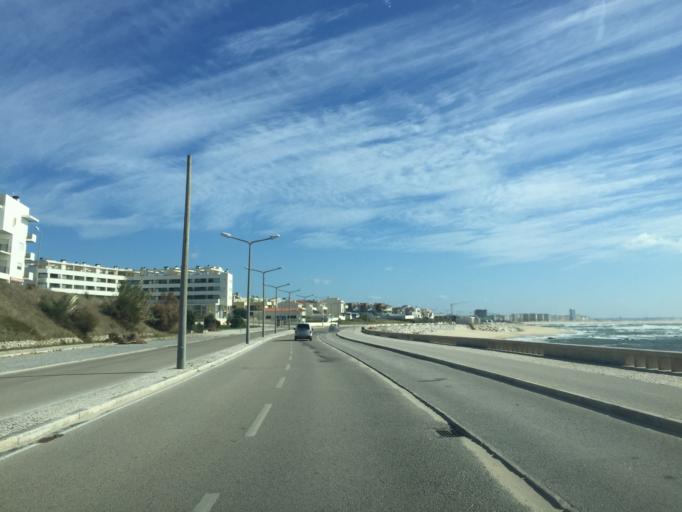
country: PT
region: Coimbra
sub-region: Figueira da Foz
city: Buarcos
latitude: 40.1713
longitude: -8.8916
